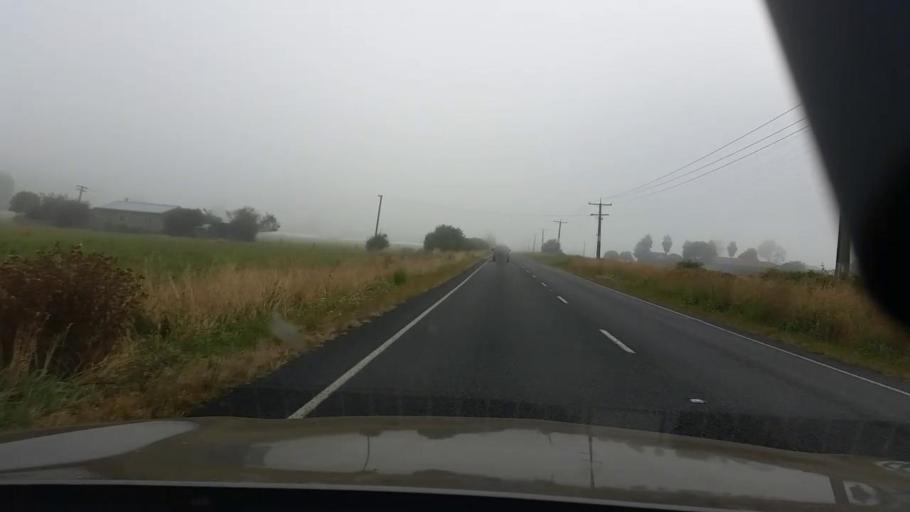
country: NZ
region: Waikato
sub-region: Waikato District
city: Ngaruawahia
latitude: -37.6368
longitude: 175.2993
